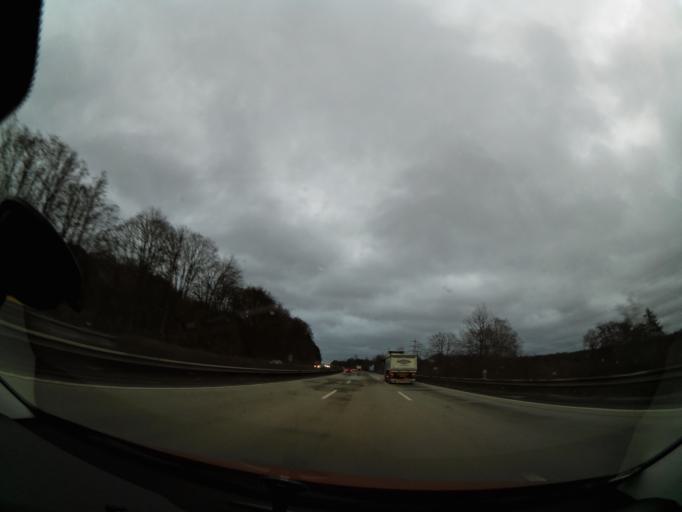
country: DE
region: Rheinland-Pfalz
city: Niederwerth
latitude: 50.4292
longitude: 7.6300
